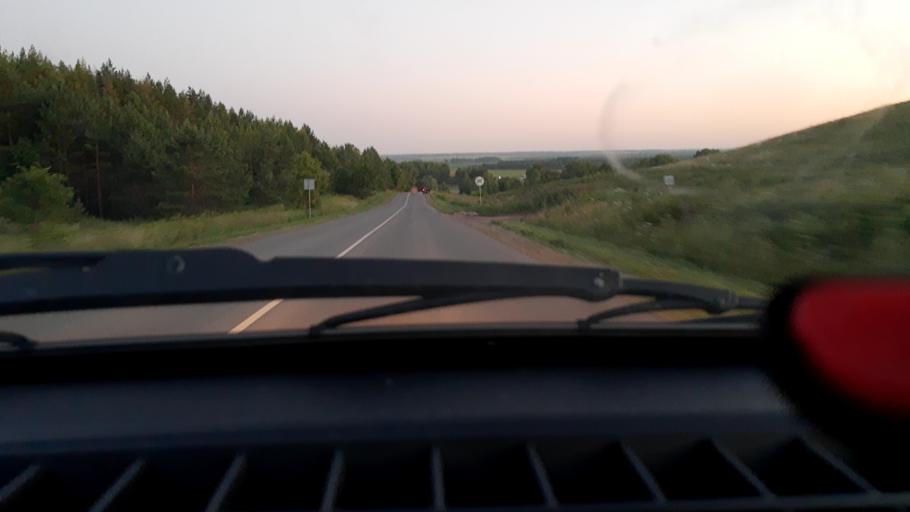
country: RU
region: Bashkortostan
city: Avdon
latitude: 54.4640
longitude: 55.8615
